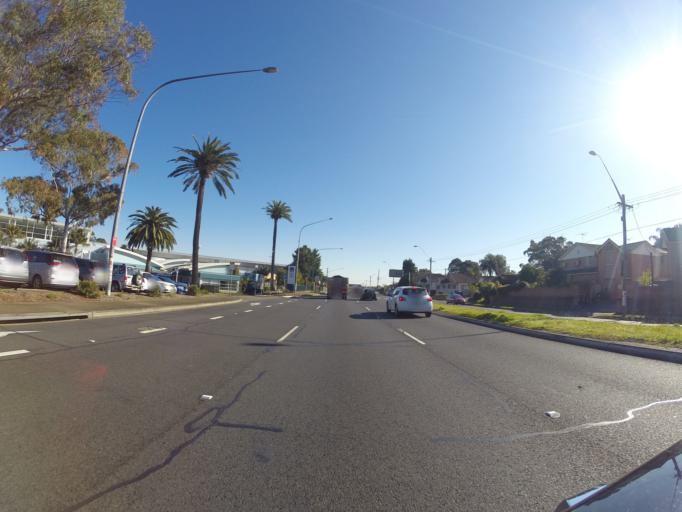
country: AU
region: New South Wales
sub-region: Hurstville
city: Penshurst
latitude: -33.9631
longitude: 151.0922
